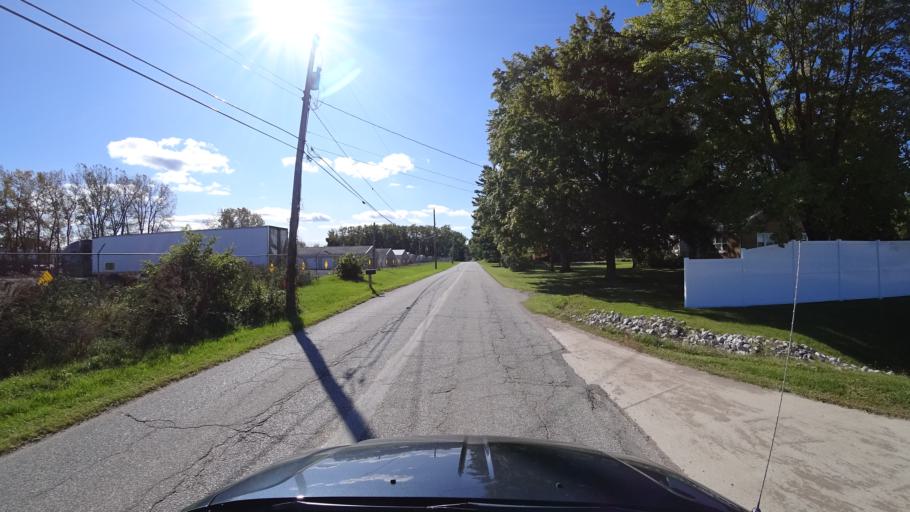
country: US
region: Indiana
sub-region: LaPorte County
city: Michigan City
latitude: 41.6798
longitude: -86.9133
